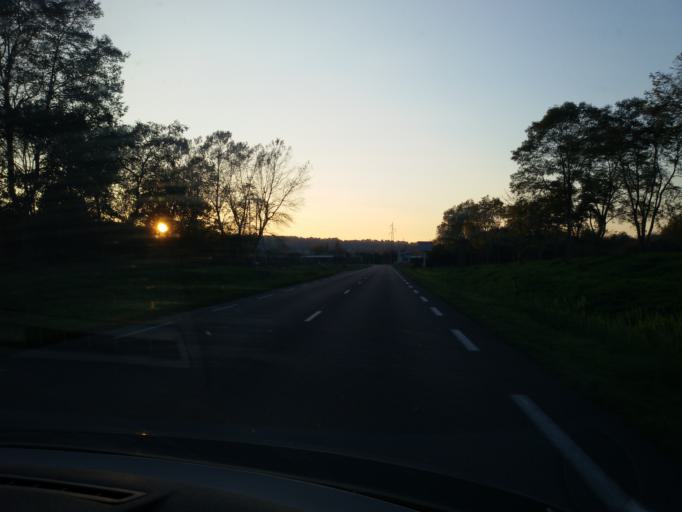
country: FR
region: Lower Normandy
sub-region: Departement du Calvados
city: La Riviere-Saint-Sauveur
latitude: 49.4126
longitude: 0.2767
